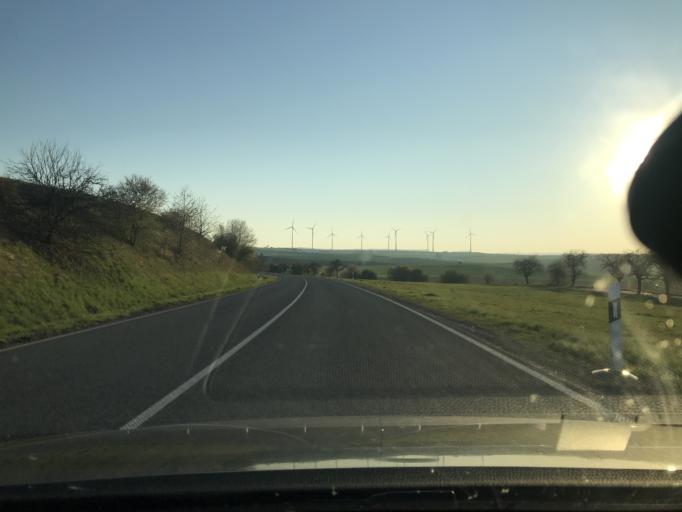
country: DE
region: Thuringia
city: Nohra
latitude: 51.4800
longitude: 10.7179
